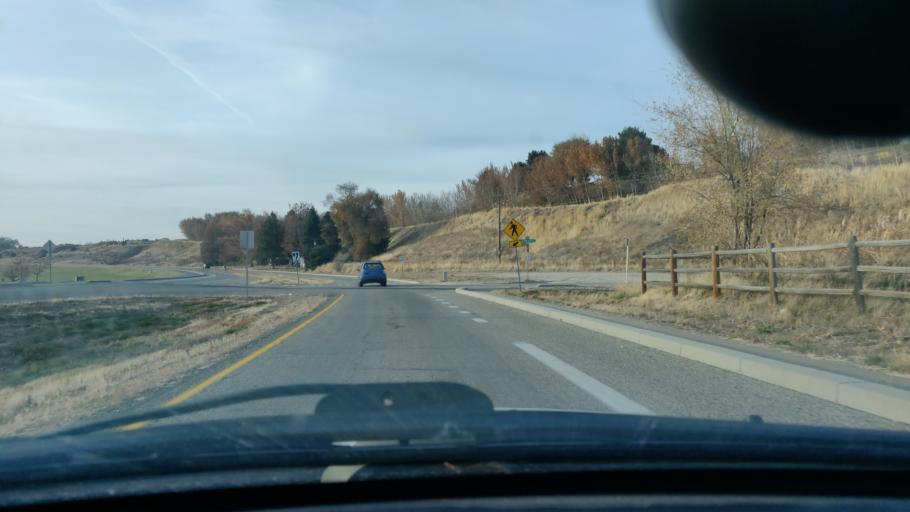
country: US
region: Idaho
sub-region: Ada County
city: Eagle
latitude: 43.6899
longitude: -116.3038
